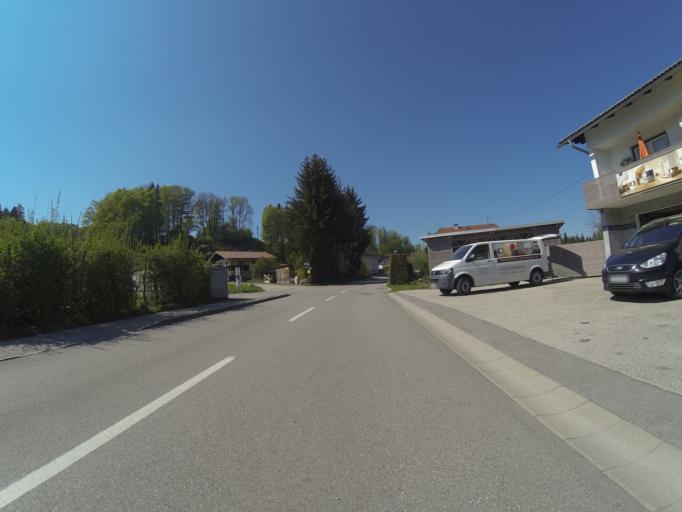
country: AT
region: Upper Austria
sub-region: Politischer Bezirk Gmunden
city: Altmunster
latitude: 47.9479
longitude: 13.7509
